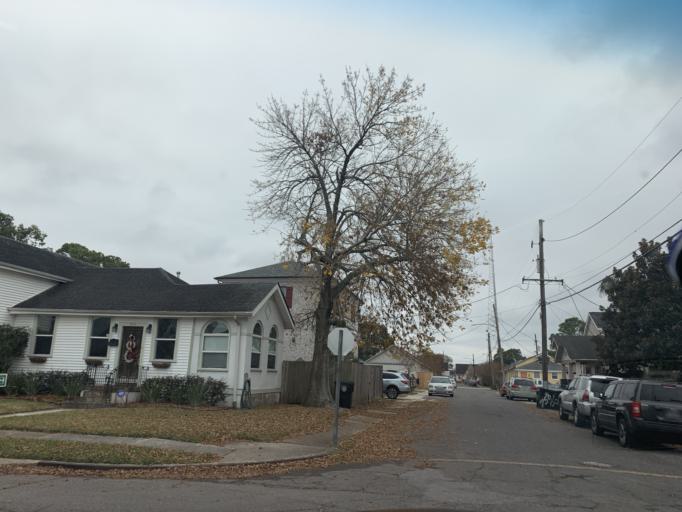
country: US
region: Louisiana
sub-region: Jefferson Parish
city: Metairie
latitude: 29.9886
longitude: -90.1081
